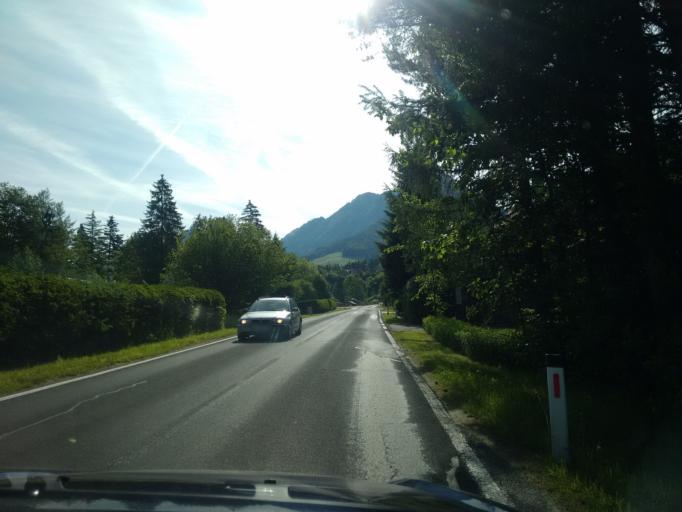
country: AT
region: Styria
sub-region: Politischer Bezirk Liezen
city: Bad Aussee
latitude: 47.6163
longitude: 13.8141
